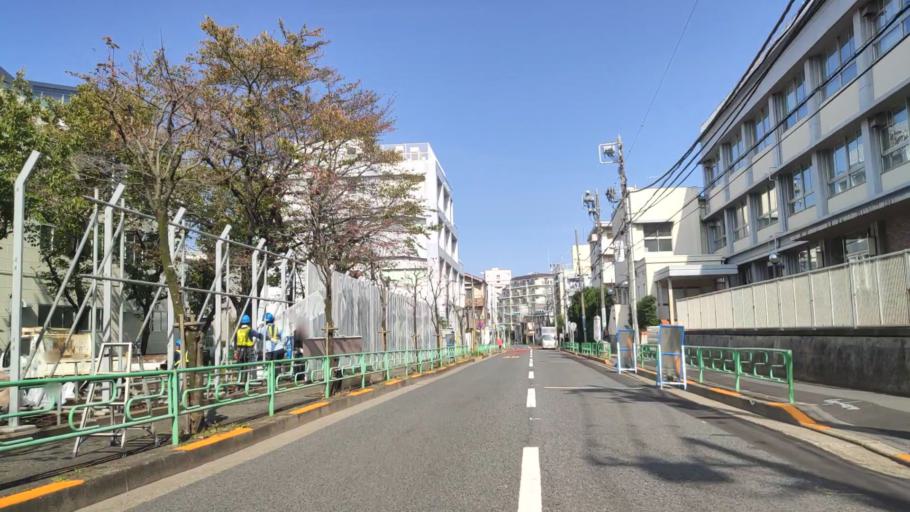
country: JP
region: Tokyo
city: Tokyo
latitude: 35.6871
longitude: 139.6653
